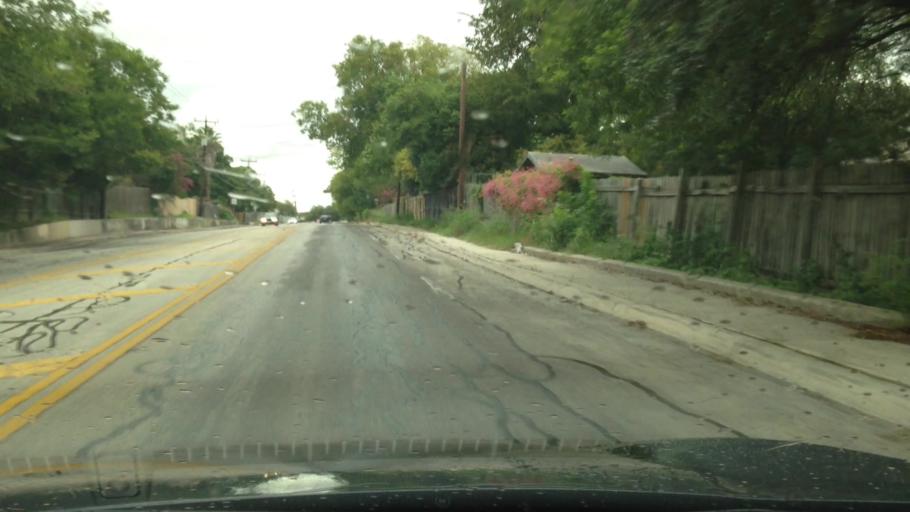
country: US
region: Texas
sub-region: Bexar County
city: Windcrest
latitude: 29.5648
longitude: -98.3971
